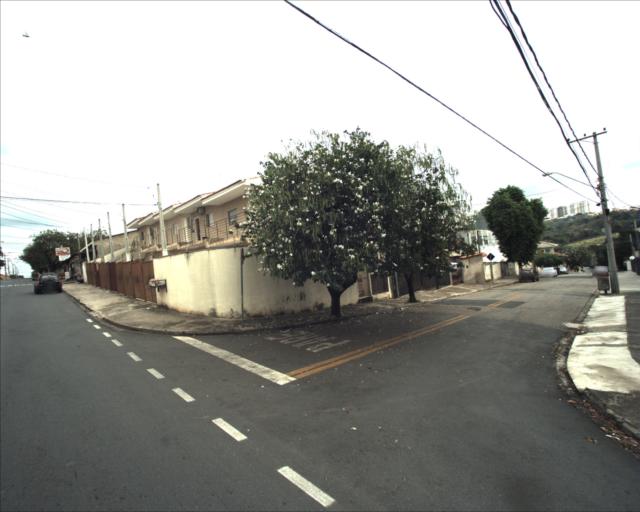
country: BR
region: Sao Paulo
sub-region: Sorocaba
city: Sorocaba
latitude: -23.4991
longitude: -47.4960
